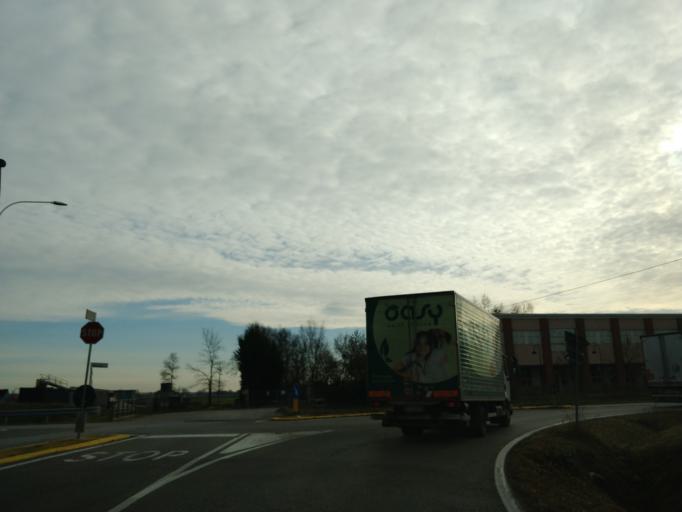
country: IT
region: Emilia-Romagna
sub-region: Provincia di Bologna
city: Argelato
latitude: 44.6355
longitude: 11.3444
